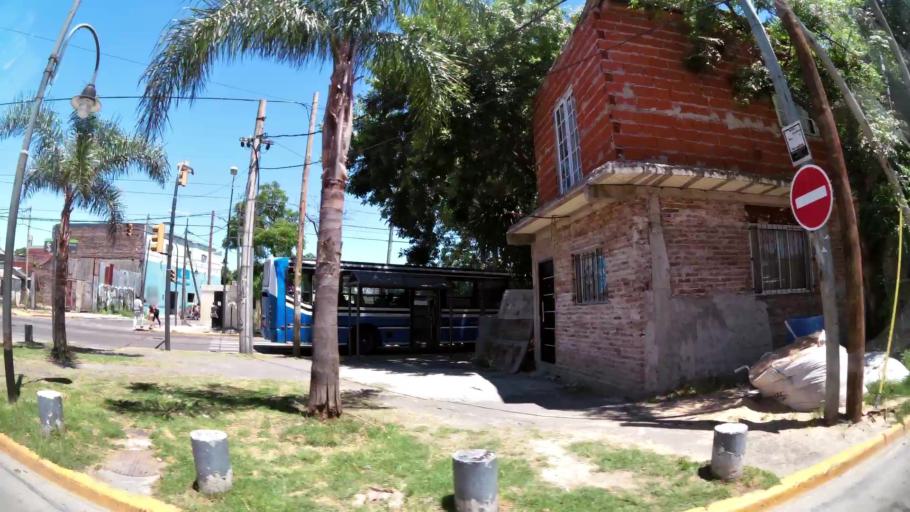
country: AR
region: Buenos Aires
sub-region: Partido de Tigre
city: Tigre
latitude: -34.4508
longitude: -58.5567
